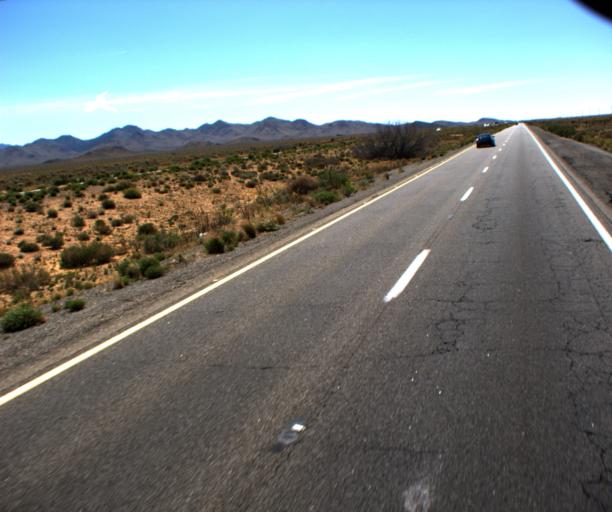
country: US
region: Arizona
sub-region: Mohave County
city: Dolan Springs
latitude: 35.4953
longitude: -114.3289
